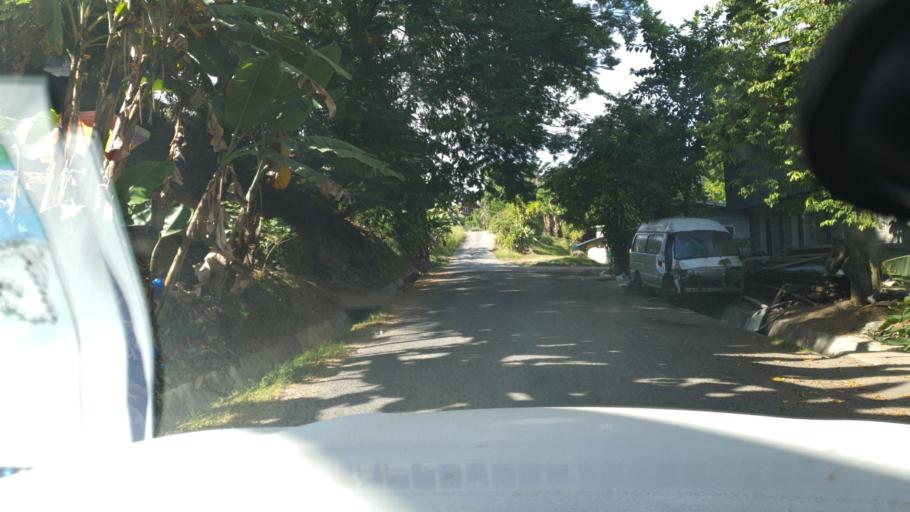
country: SB
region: Guadalcanal
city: Honiara
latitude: -9.4362
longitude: 159.9525
